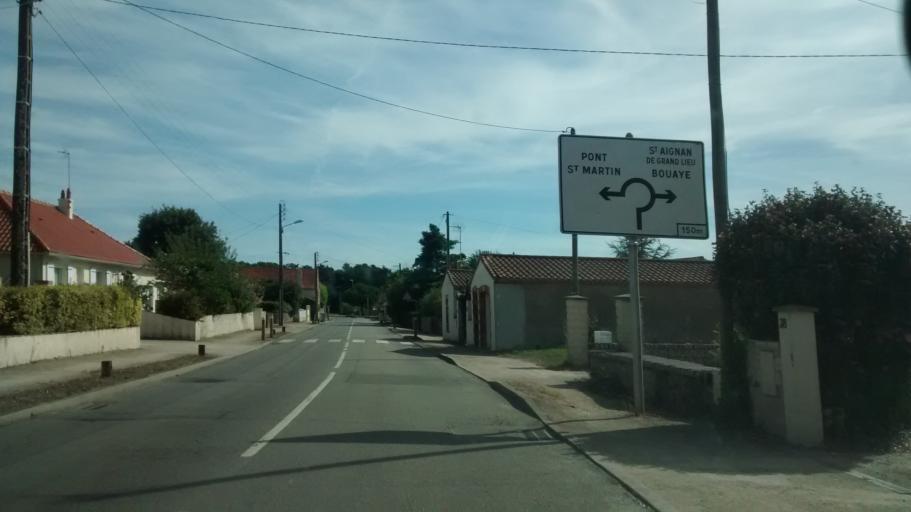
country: FR
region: Pays de la Loire
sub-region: Departement de la Loire-Atlantique
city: Pont-Saint-Martin
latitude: 47.1261
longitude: -1.6180
